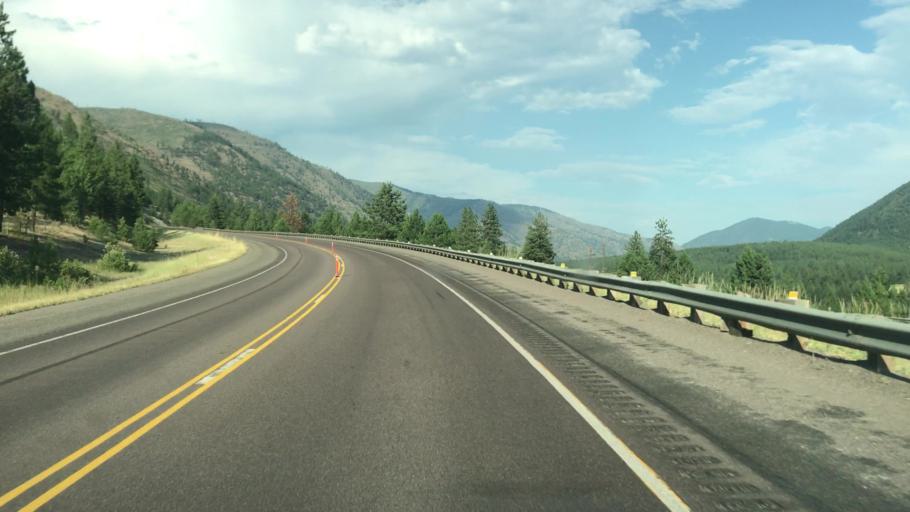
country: US
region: Montana
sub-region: Mineral County
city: Superior
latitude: 47.0135
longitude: -114.6965
